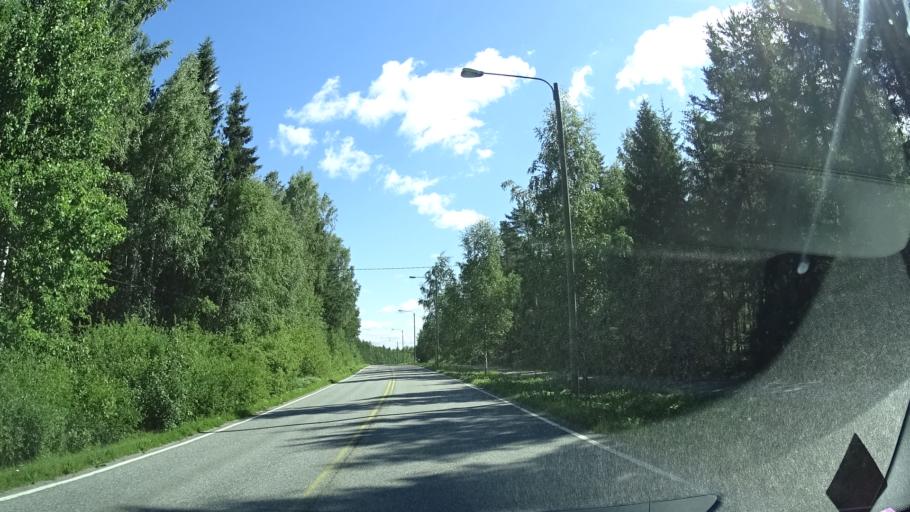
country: FI
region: Varsinais-Suomi
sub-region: Turku
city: Lemu
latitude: 60.5712
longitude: 21.9465
